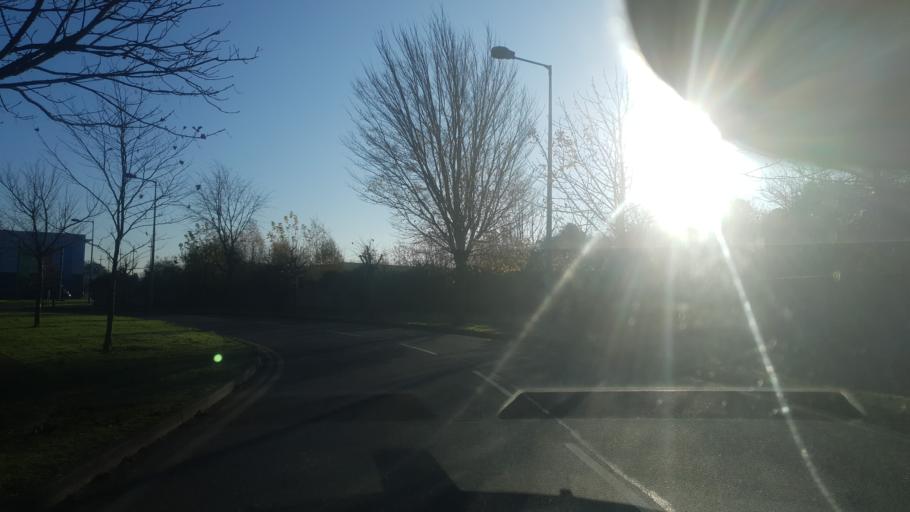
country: IE
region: Munster
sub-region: Ciarrai
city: Tralee
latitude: 52.2627
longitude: -9.6805
